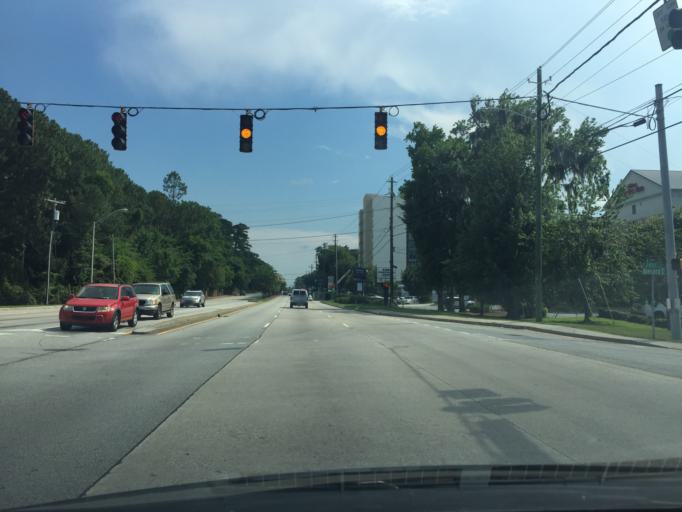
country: US
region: Georgia
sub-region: Chatham County
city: Savannah
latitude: 32.0234
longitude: -81.1101
